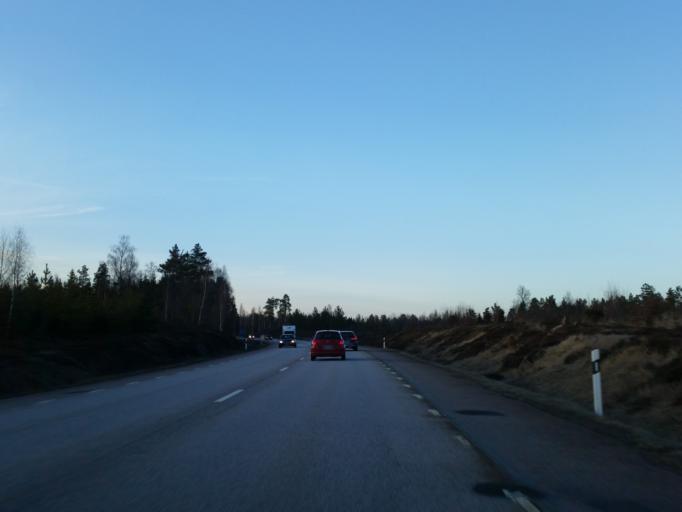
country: SE
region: Kalmar
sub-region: Oskarshamns Kommun
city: Oskarshamn
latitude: 57.4877
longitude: 16.5183
